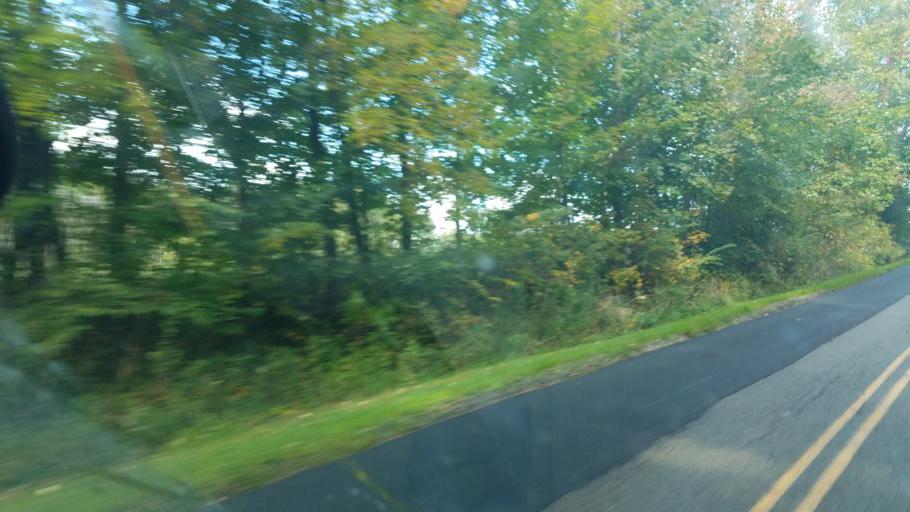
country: US
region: Ohio
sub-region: Knox County
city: Fredericktown
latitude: 40.4884
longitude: -82.5128
